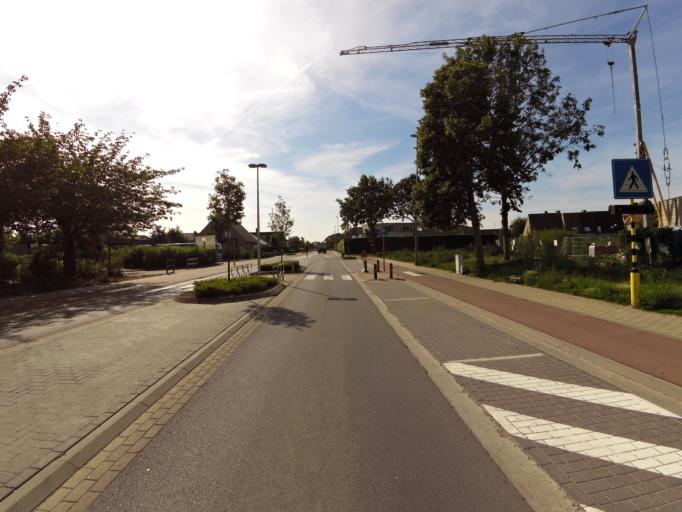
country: BE
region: Flanders
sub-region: Provincie West-Vlaanderen
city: Koekelare
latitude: 51.0921
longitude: 2.9804
